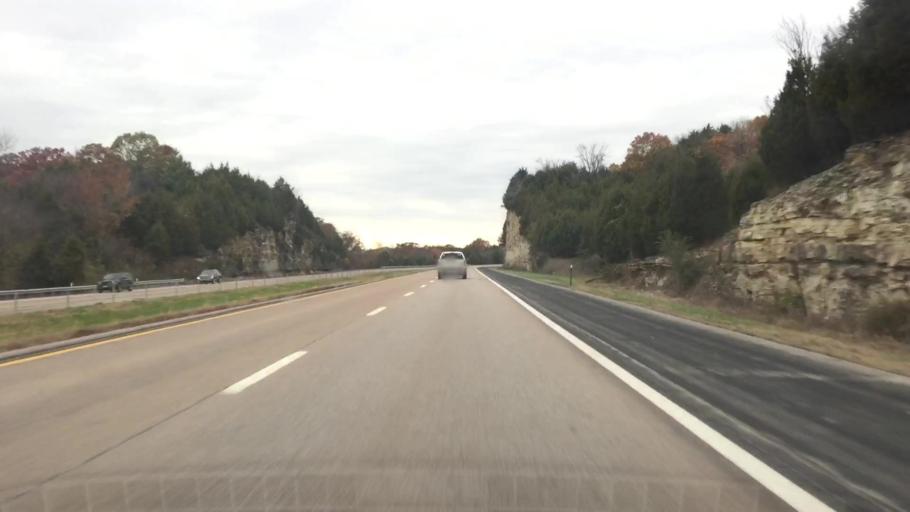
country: US
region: Missouri
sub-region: Boone County
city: Ashland
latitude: 38.6775
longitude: -92.2481
